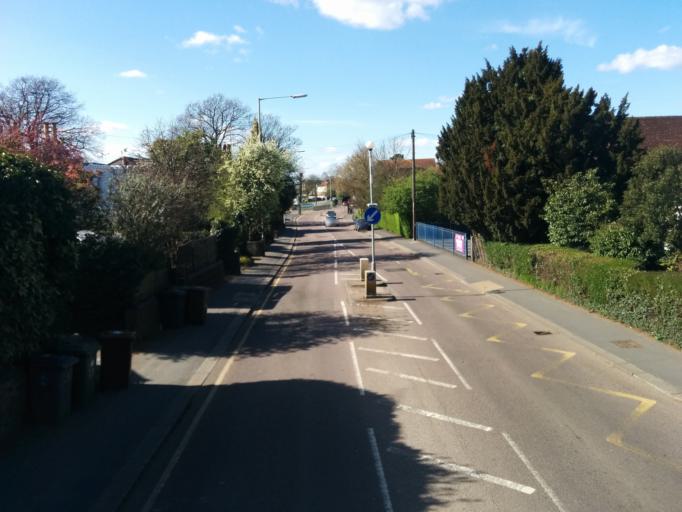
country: GB
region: England
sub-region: Hertfordshire
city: Bushey
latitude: 51.6415
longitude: -0.3586
